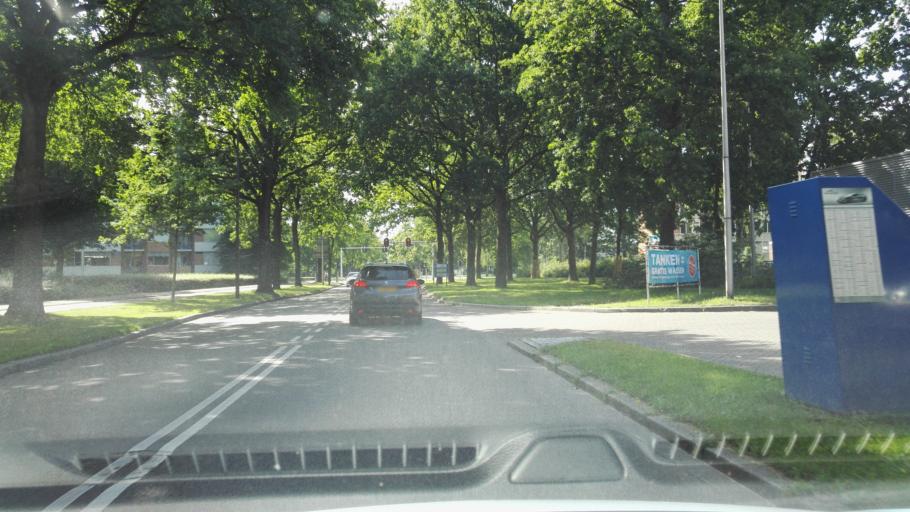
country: NL
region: Gelderland
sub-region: Gemeente Apeldoorn
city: Apeldoorn
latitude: 52.1937
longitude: 5.9761
